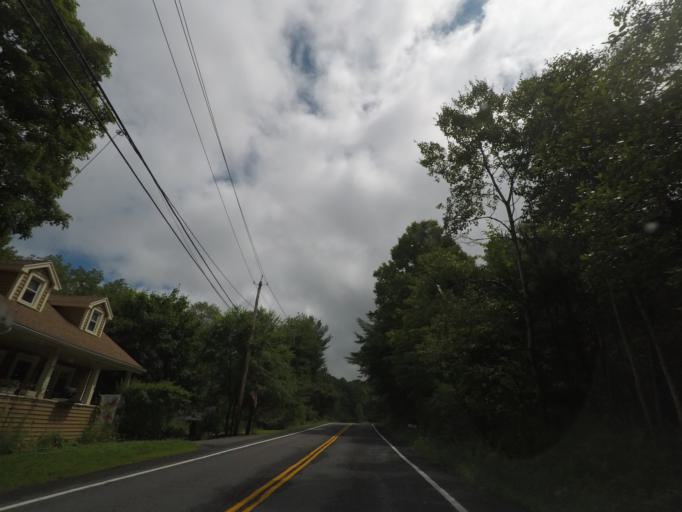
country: US
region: New York
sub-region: Rensselaer County
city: Averill Park
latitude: 42.5954
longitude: -73.5080
